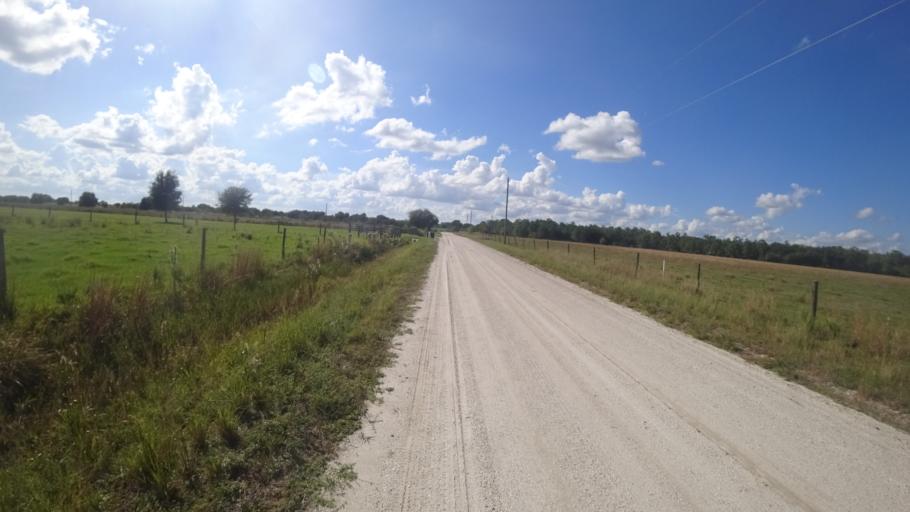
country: US
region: Florida
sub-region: Hardee County
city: Wauchula
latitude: 27.4623
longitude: -82.0536
